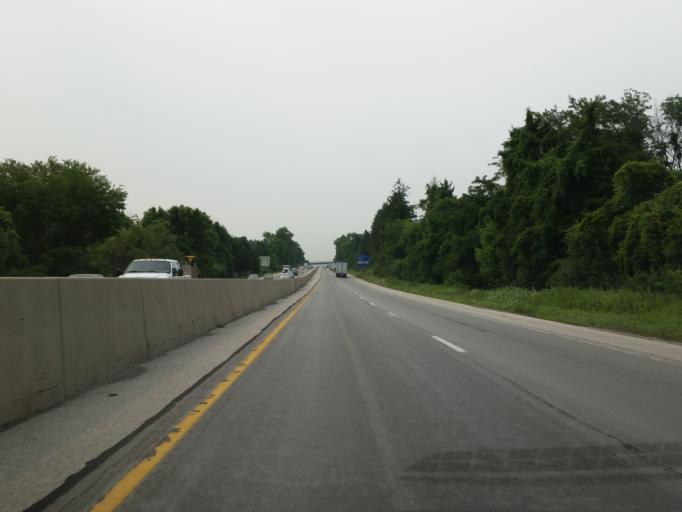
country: US
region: Pennsylvania
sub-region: York County
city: Emigsville
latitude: 40.0136
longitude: -76.7407
